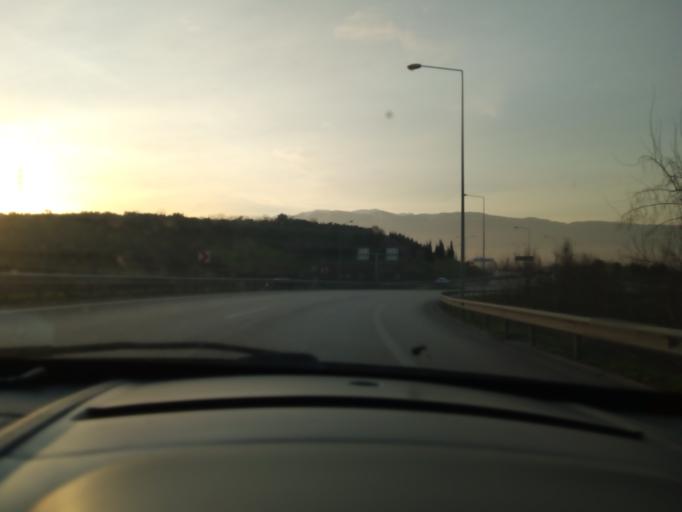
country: TR
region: Bursa
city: Demirtas
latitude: 40.2848
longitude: 29.0403
